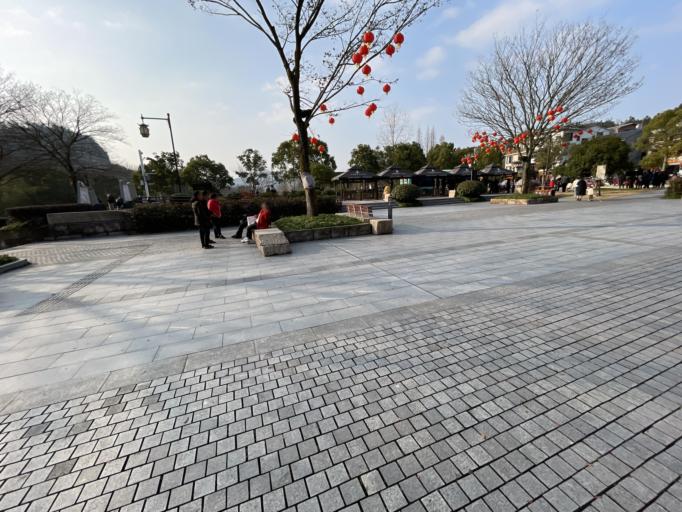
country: CN
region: Zhejiang Sheng
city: Shuhong
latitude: 28.6939
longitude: 120.1326
